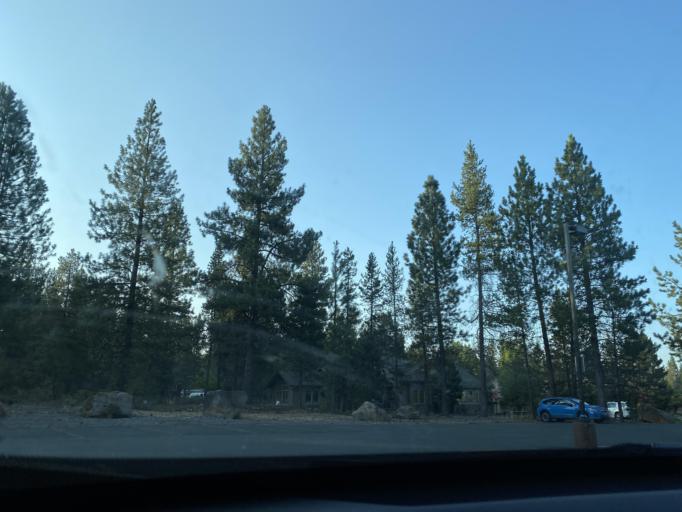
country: US
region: Oregon
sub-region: Deschutes County
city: Sunriver
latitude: 43.8748
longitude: -121.4349
